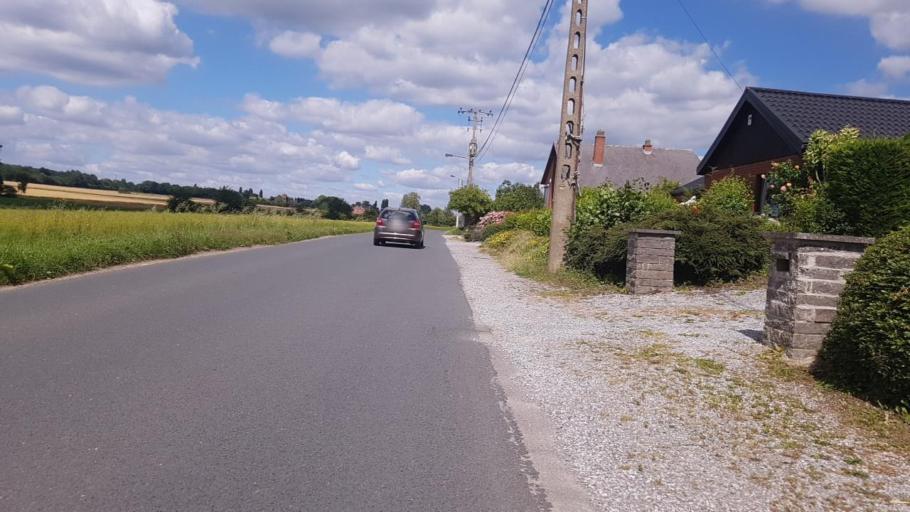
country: BE
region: Wallonia
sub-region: Province de Namur
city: Walcourt
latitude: 50.3308
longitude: 4.3842
